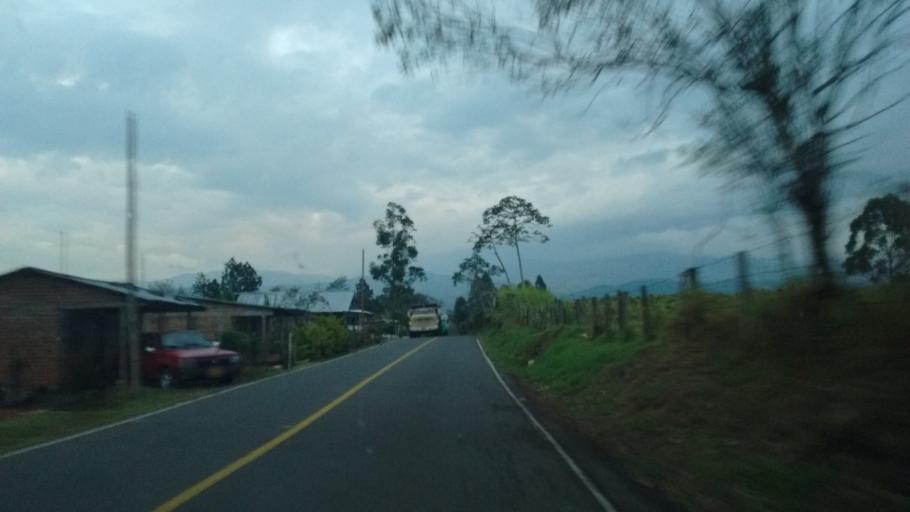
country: CO
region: Cauca
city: Popayan
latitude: 2.3704
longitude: -76.6956
